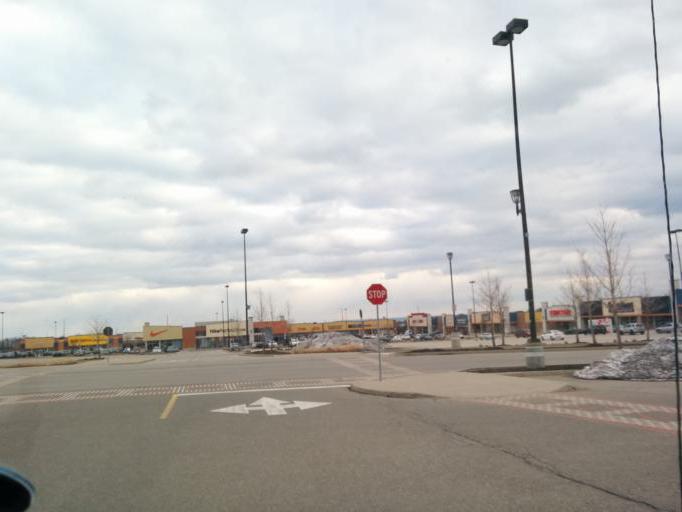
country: CA
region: Ontario
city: Oakville
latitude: 43.3977
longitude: -79.7510
